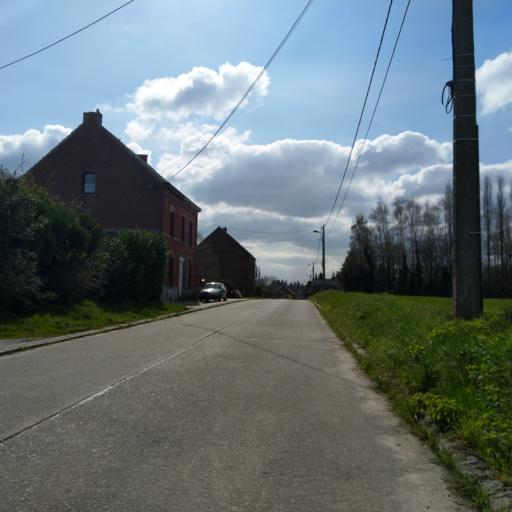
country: BE
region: Wallonia
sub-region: Province du Hainaut
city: Jurbise
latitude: 50.5419
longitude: 3.9581
